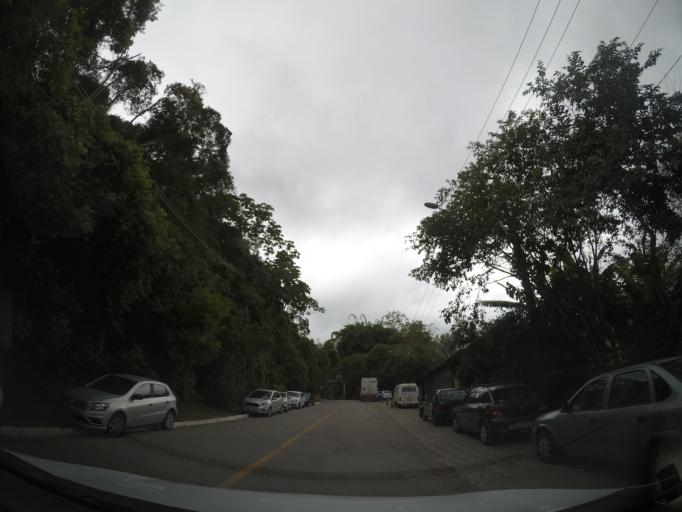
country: BR
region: Sao Paulo
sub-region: Aruja
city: Aruja
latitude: -23.3302
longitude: -46.4004
